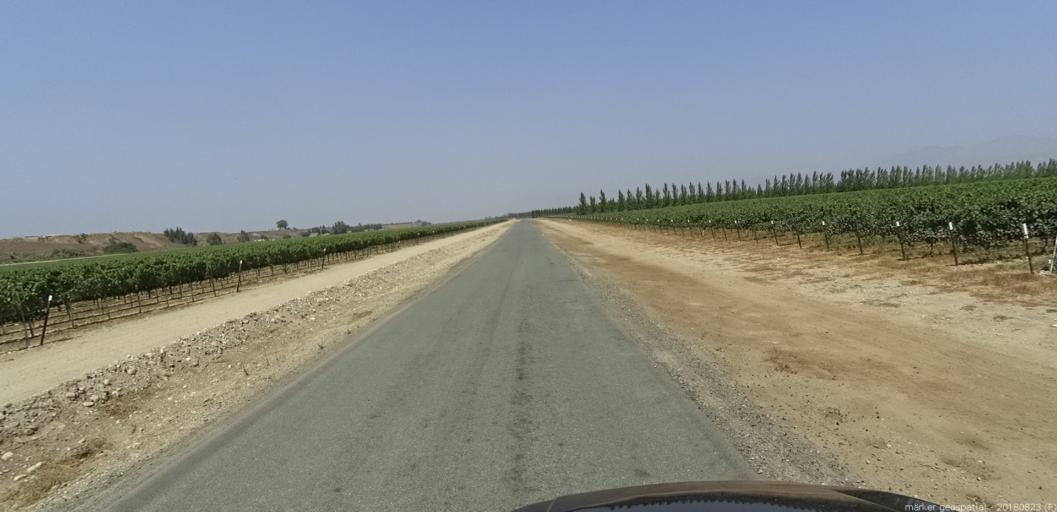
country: US
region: California
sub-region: Monterey County
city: Greenfield
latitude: 36.3348
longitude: -121.2967
